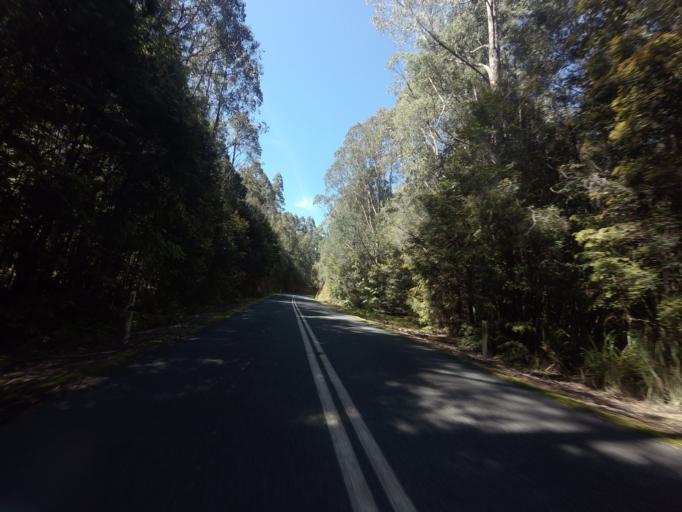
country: AU
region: Tasmania
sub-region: Huon Valley
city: Geeveston
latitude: -42.8200
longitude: 146.3029
